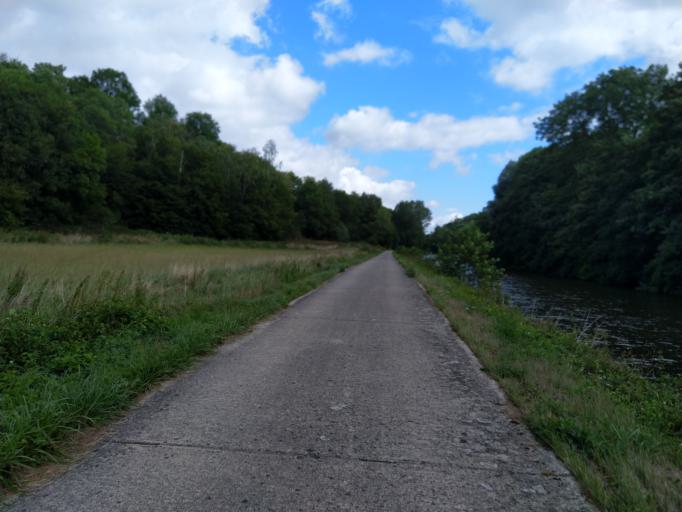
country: BE
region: Wallonia
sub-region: Province du Hainaut
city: Lobbes
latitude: 50.3393
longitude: 4.2436
